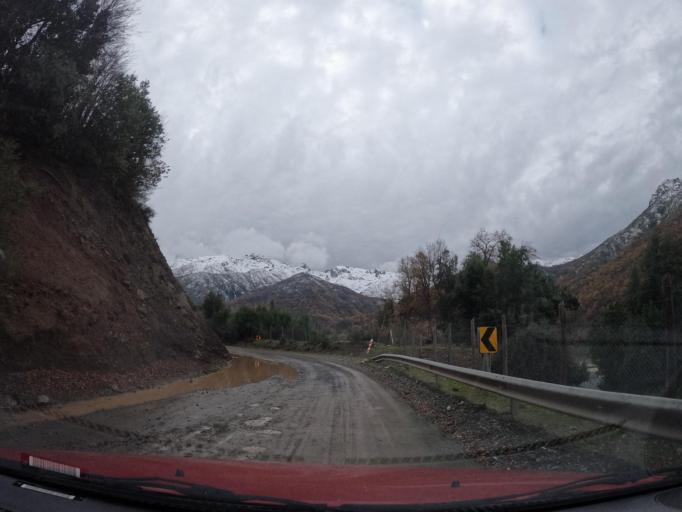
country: CL
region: Maule
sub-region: Provincia de Linares
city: Colbun
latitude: -35.8608
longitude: -71.1308
